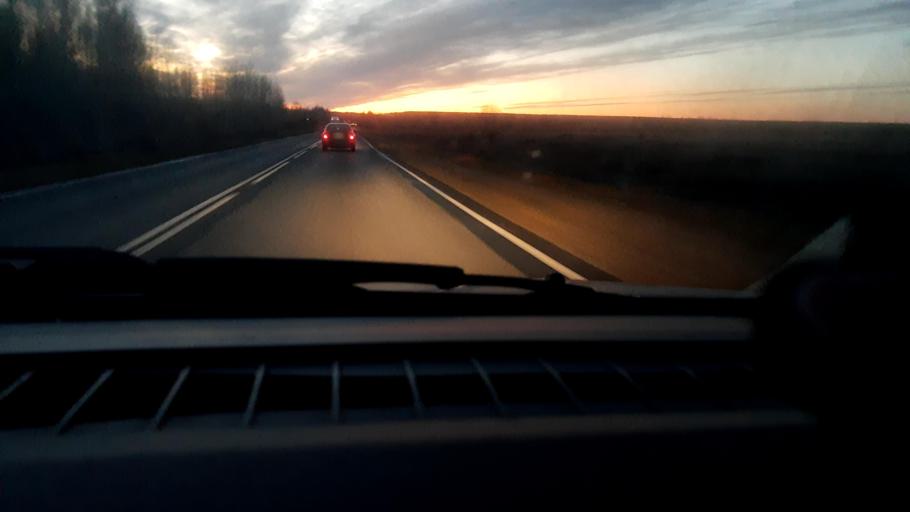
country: RU
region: Nizjnij Novgorod
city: Sukhobezvodnoye
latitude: 56.8597
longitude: 44.8682
